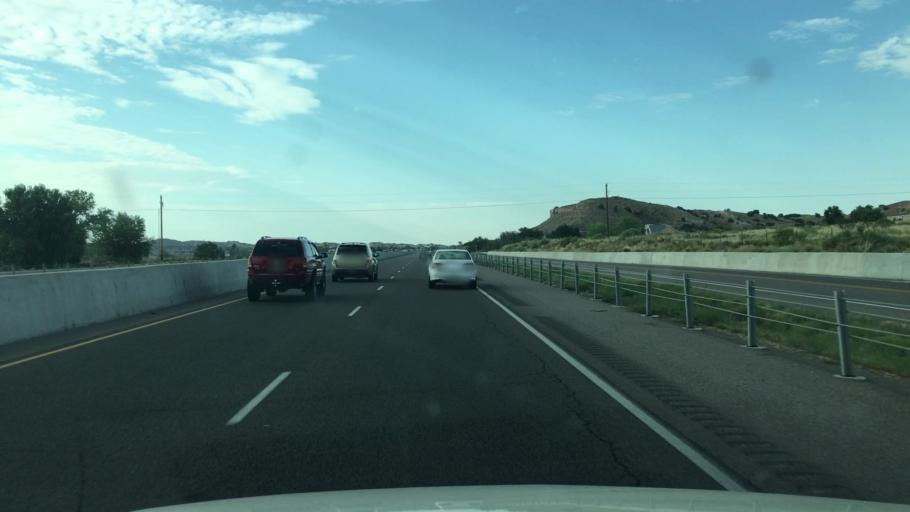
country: US
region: New Mexico
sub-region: Santa Fe County
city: El Valle de Arroyo Seco
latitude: 35.9513
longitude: -106.0210
